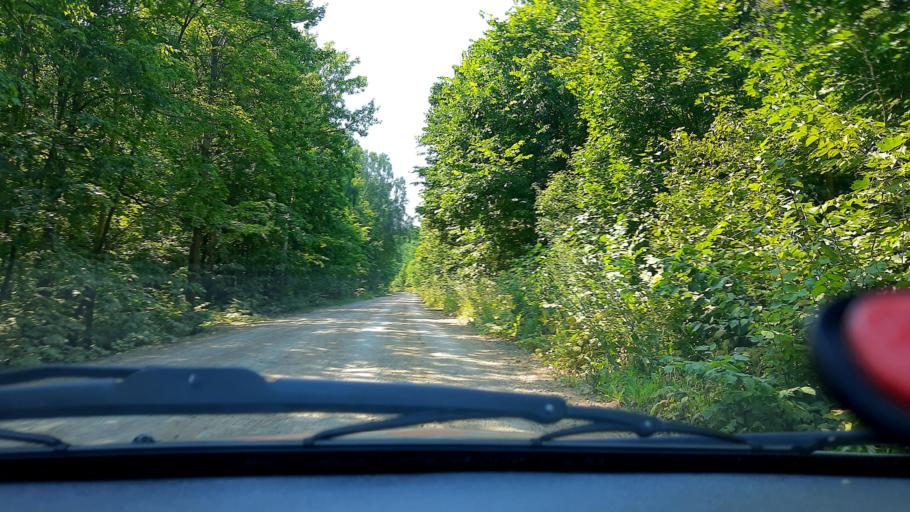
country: RU
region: Bashkortostan
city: Karmaskaly
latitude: 54.3900
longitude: 55.8989
